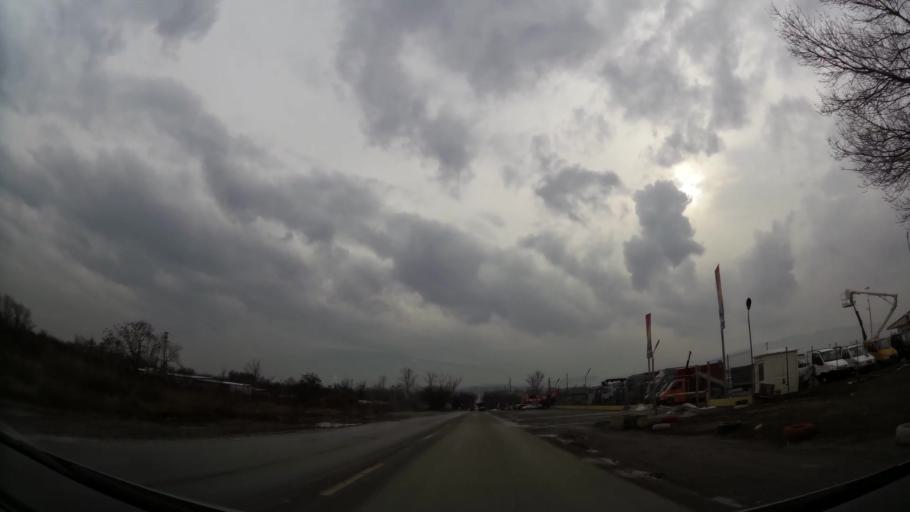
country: BG
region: Sofiya
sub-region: Obshtina Bozhurishte
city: Bozhurishte
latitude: 42.7050
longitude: 23.2303
